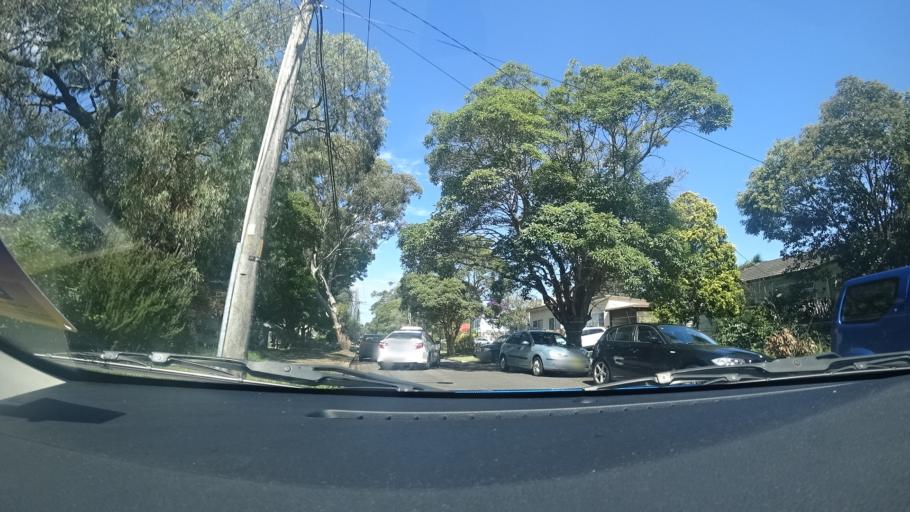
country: AU
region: New South Wales
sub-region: Warringah
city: Allambie Heights
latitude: -33.7604
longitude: 151.2483
